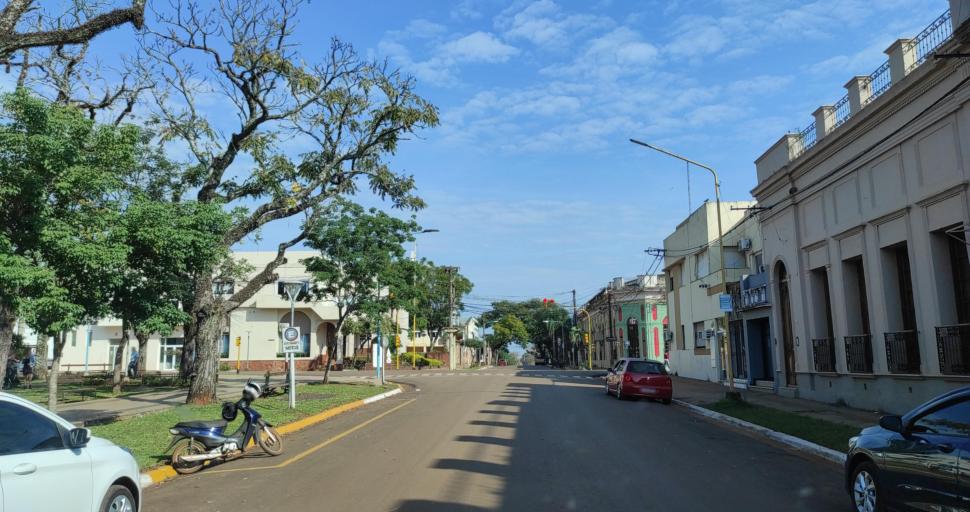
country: AR
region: Corrientes
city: Santo Tome
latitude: -28.5497
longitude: -56.0356
